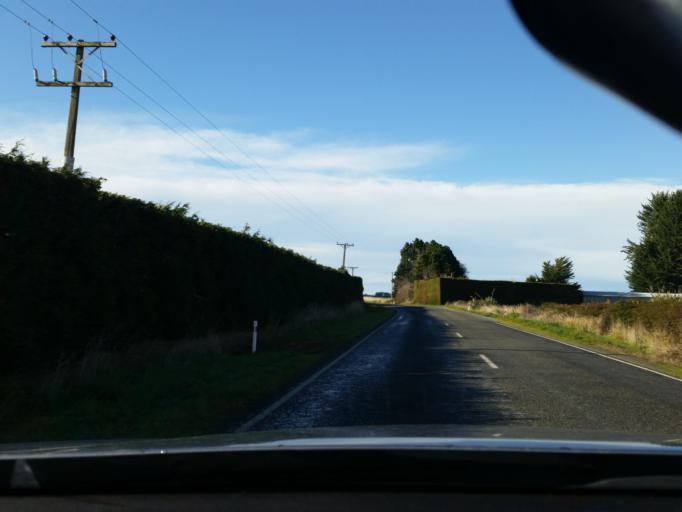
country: NZ
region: Southland
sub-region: Southland District
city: Riverton
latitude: -46.1535
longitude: 168.0459
